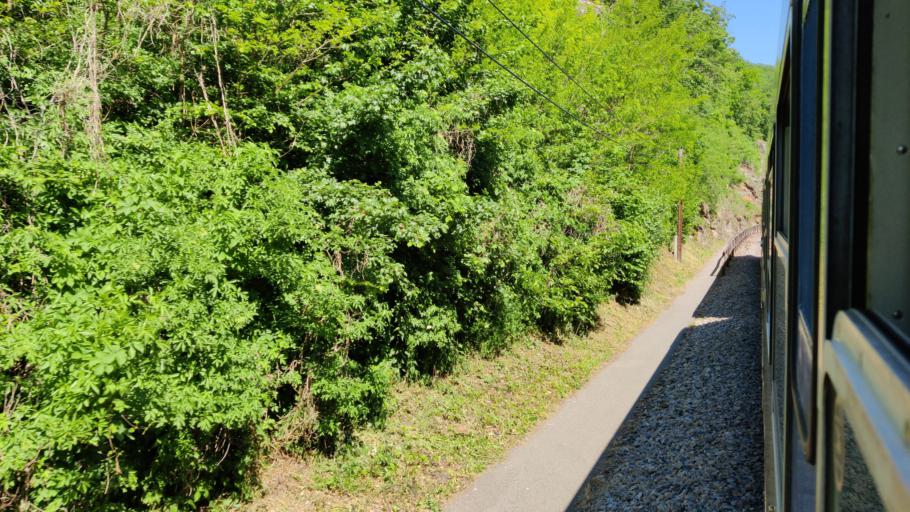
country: AT
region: Lower Austria
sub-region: Politischer Bezirk Horn
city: Gars am Kamp
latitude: 48.6021
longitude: 15.6537
